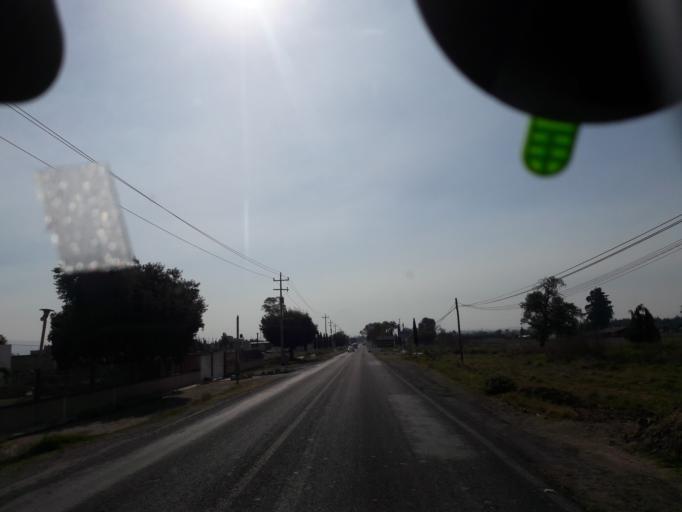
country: MX
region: Tlaxcala
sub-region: Ixtacuixtla de Mariano Matamoros
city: Villa Mariano Matamoros
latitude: 19.3101
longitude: -98.3826
